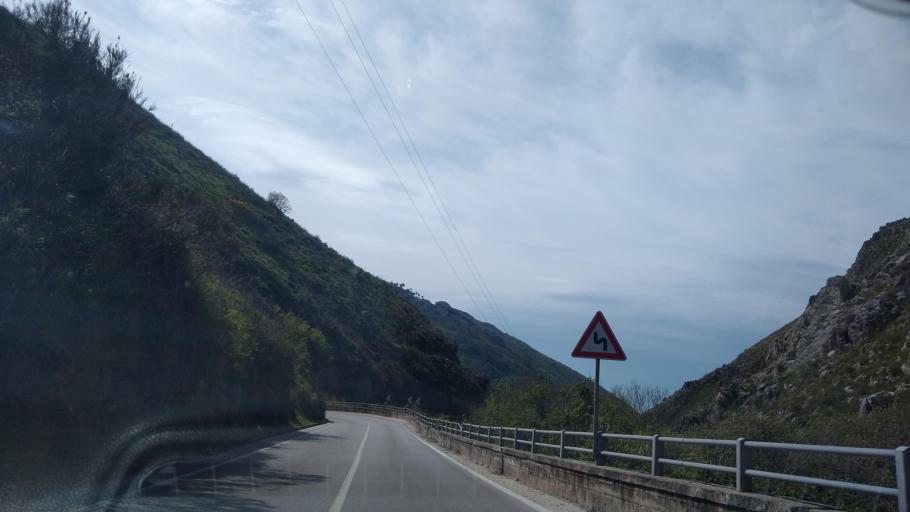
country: IT
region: Sicily
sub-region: Palermo
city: Pioppo
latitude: 38.0493
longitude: 13.1946
